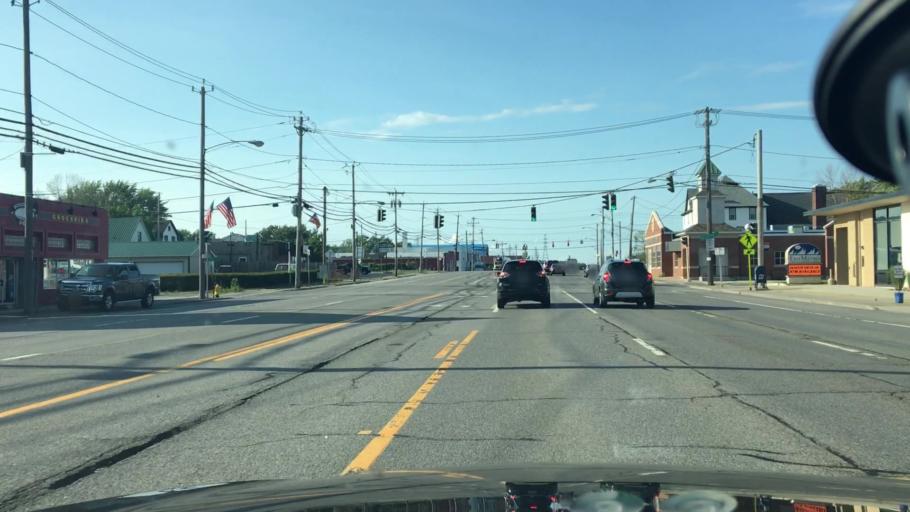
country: US
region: New York
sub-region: Erie County
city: Blasdell
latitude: 42.7960
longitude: -78.8468
